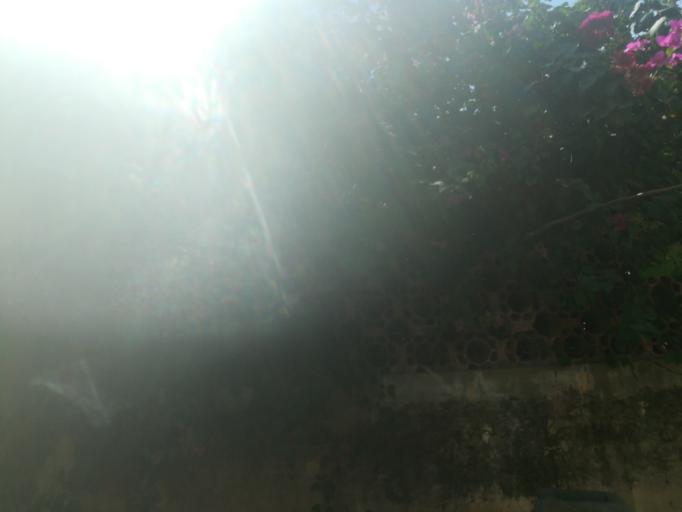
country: NG
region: Kano
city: Kano
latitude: 12.0294
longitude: 8.5151
